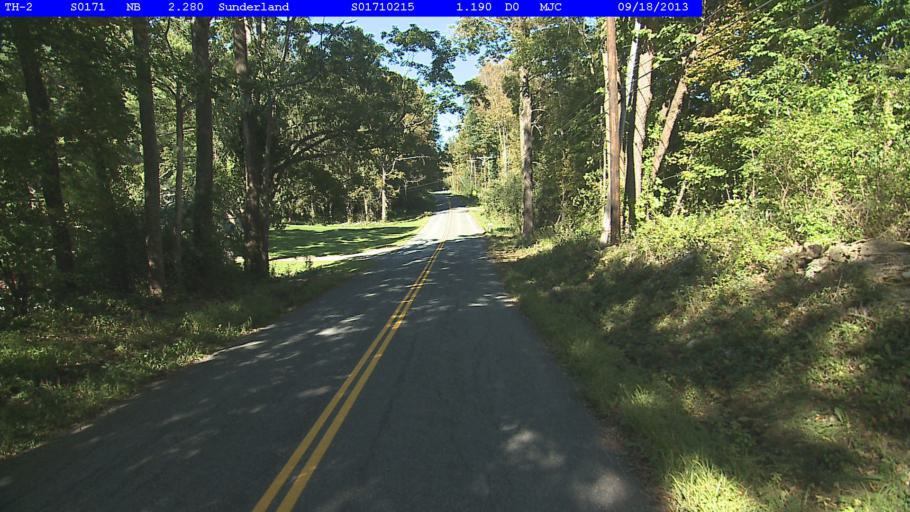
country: US
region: Vermont
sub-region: Bennington County
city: Arlington
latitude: 43.0822
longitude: -73.1264
